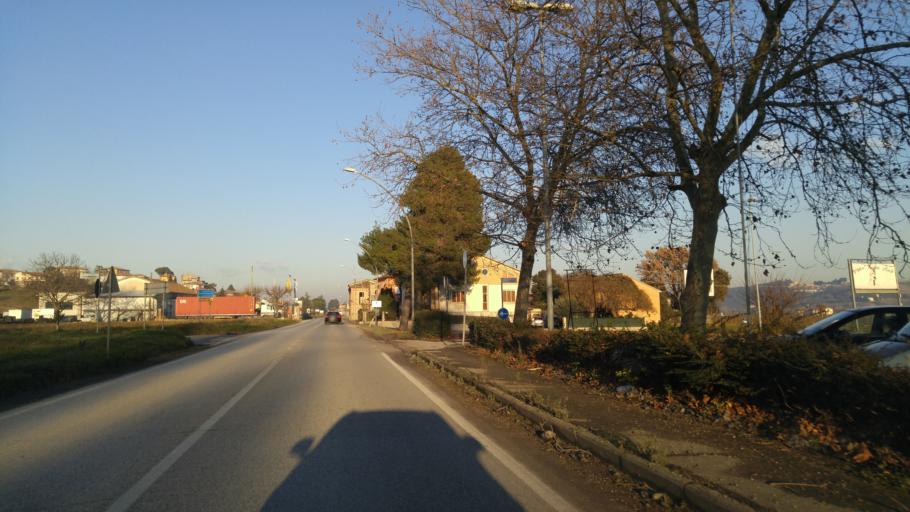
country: IT
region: The Marches
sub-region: Provincia di Pesaro e Urbino
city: Monte Porzio
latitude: 43.6926
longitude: 13.0530
